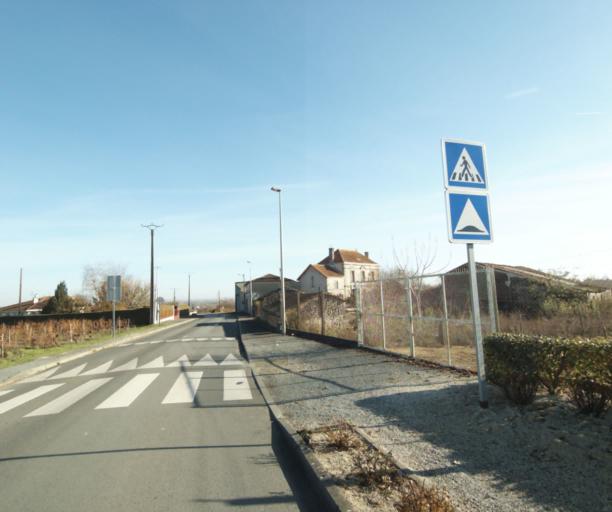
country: FR
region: Poitou-Charentes
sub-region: Departement de la Charente-Maritime
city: Burie
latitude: 45.7768
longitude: -0.4141
